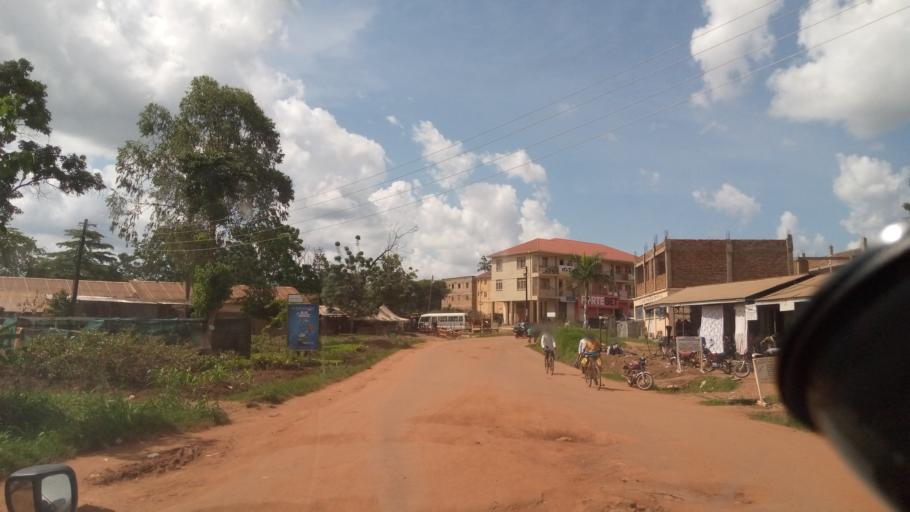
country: UG
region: Northern Region
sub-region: Lira District
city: Lira
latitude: 2.2465
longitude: 32.8975
